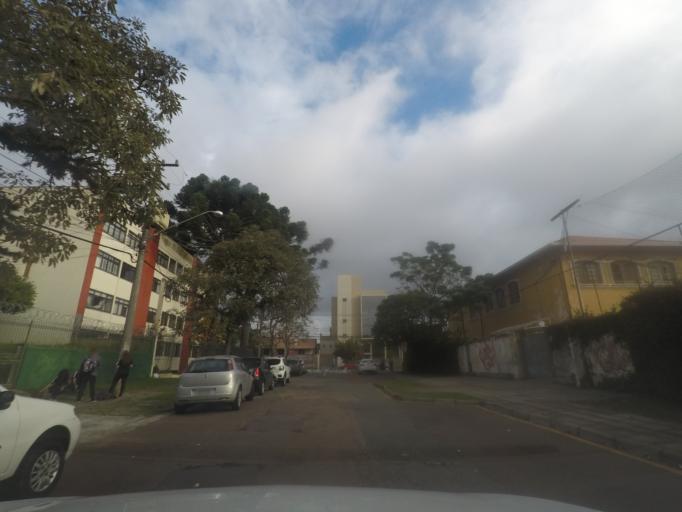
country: BR
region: Parana
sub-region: Curitiba
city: Curitiba
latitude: -25.4309
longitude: -49.2451
